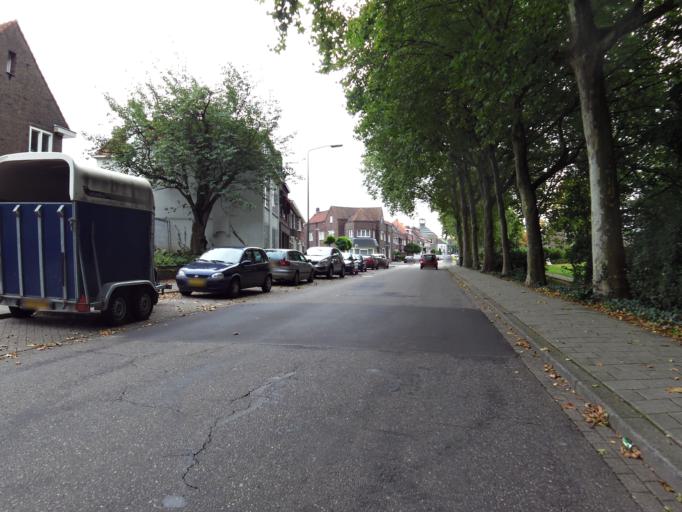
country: NL
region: Limburg
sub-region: Gemeente Heerlen
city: Heerlen
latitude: 50.8968
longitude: 5.9805
